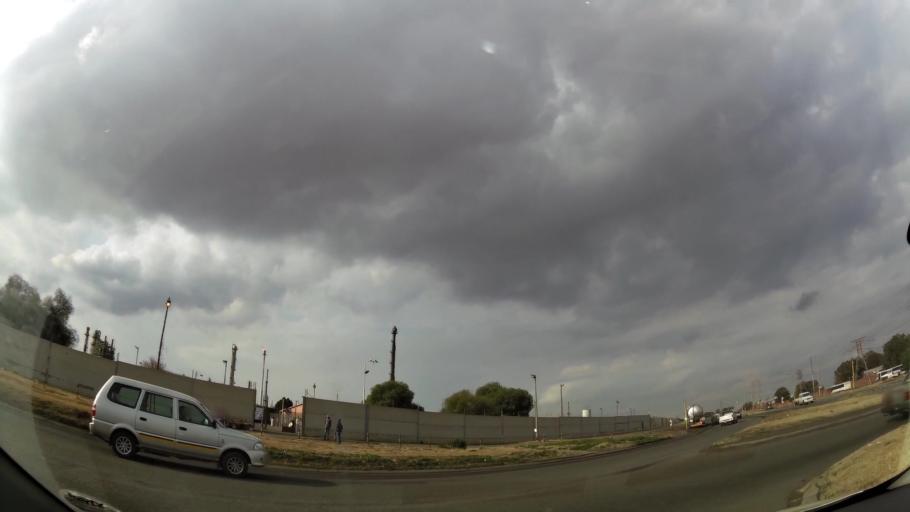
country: ZA
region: Orange Free State
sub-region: Fezile Dabi District Municipality
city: Sasolburg
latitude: -26.8345
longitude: 27.8429
